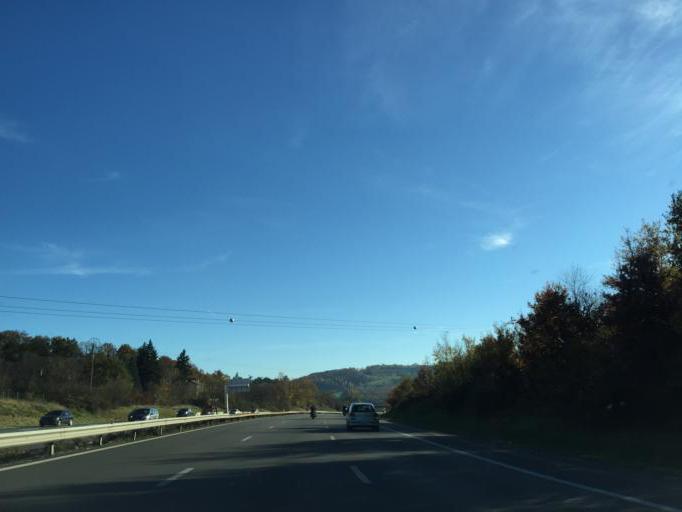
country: FR
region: Rhone-Alpes
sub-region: Departement de la Loire
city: La Fouillouse
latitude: 45.5143
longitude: 4.3005
